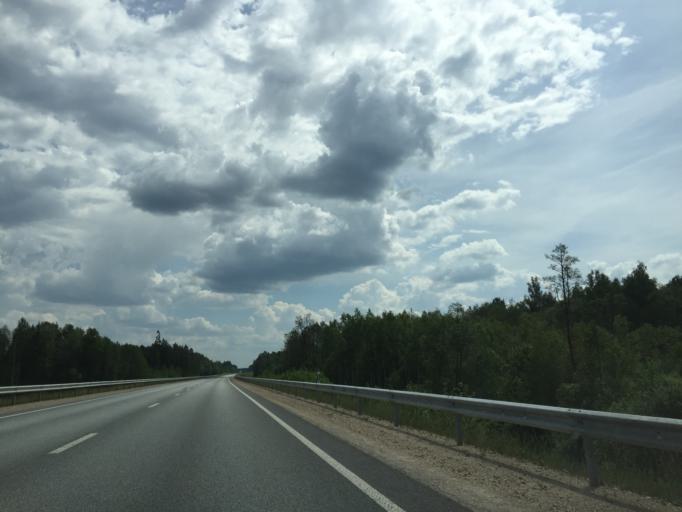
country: LV
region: Skriveri
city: Skriveri
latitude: 56.7215
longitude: 25.1923
